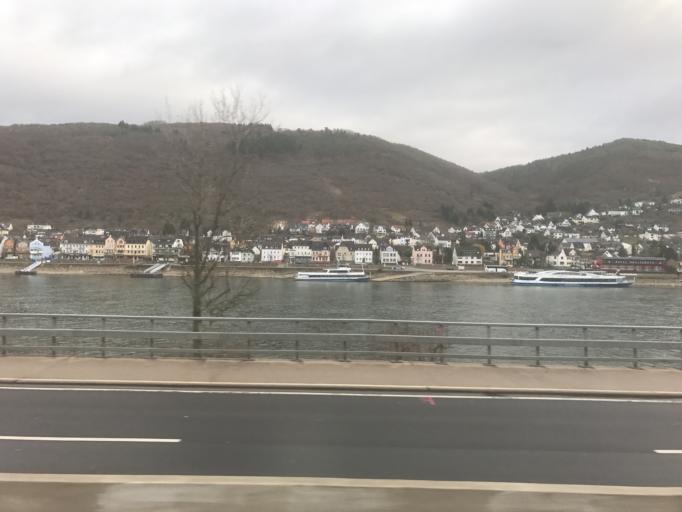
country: DE
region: Rheinland-Pfalz
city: Kamp-Bornhofen
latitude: 50.2239
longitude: 7.6139
